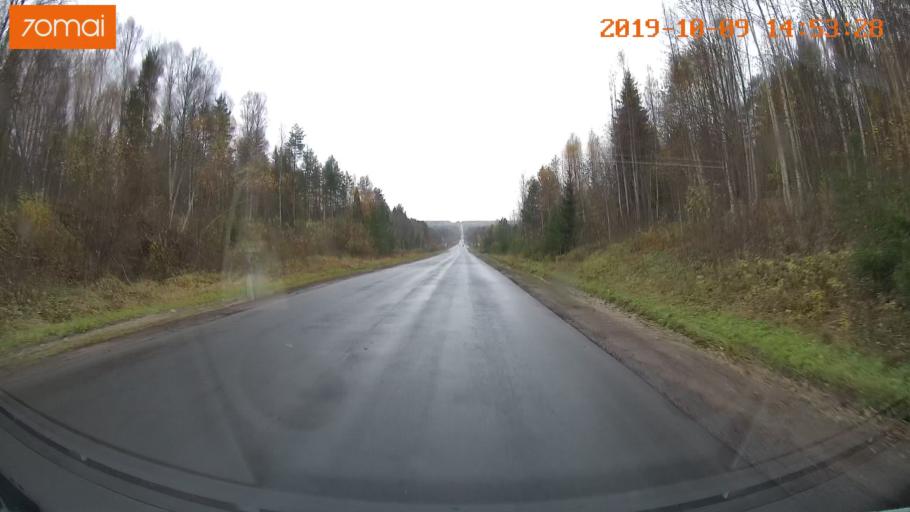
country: RU
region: Kostroma
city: Chistyye Bory
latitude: 58.3673
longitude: 41.6385
